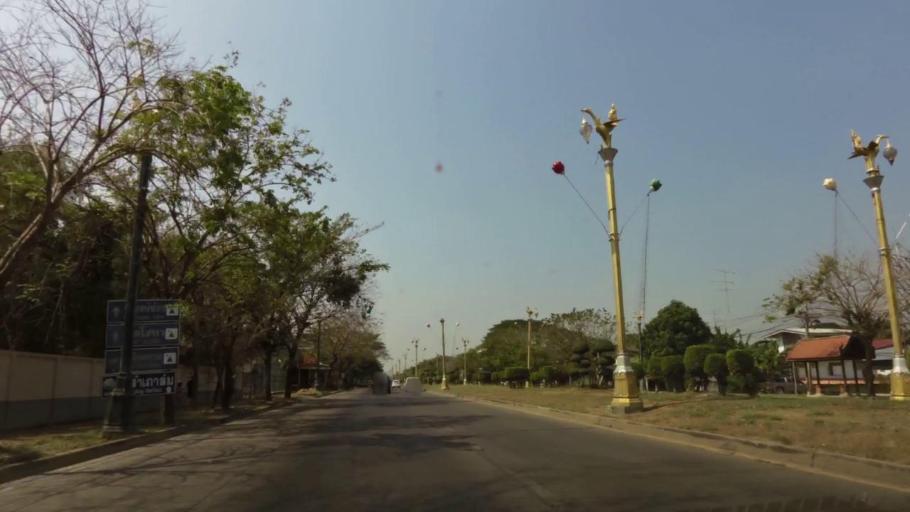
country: TH
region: Phra Nakhon Si Ayutthaya
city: Phra Nakhon Si Ayutthaya
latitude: 14.3405
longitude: 100.5685
